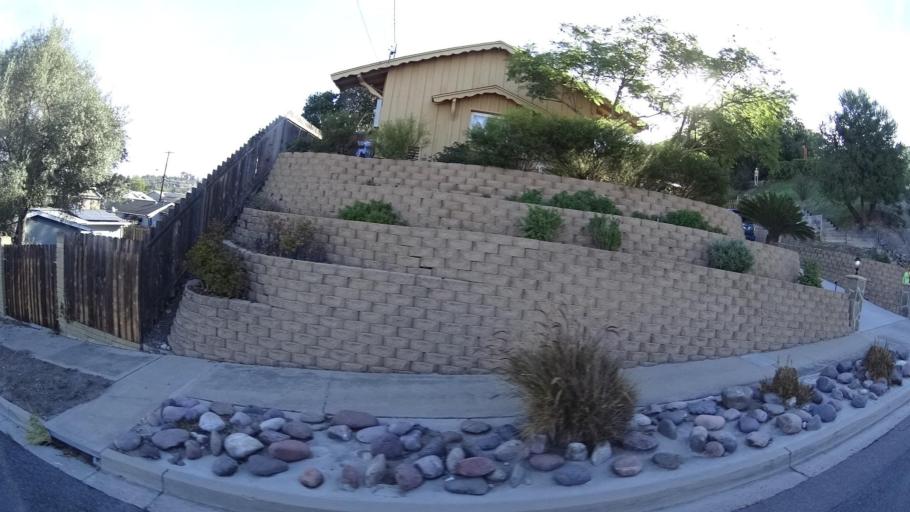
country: US
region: California
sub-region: San Diego County
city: Spring Valley
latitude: 32.7415
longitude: -116.9791
